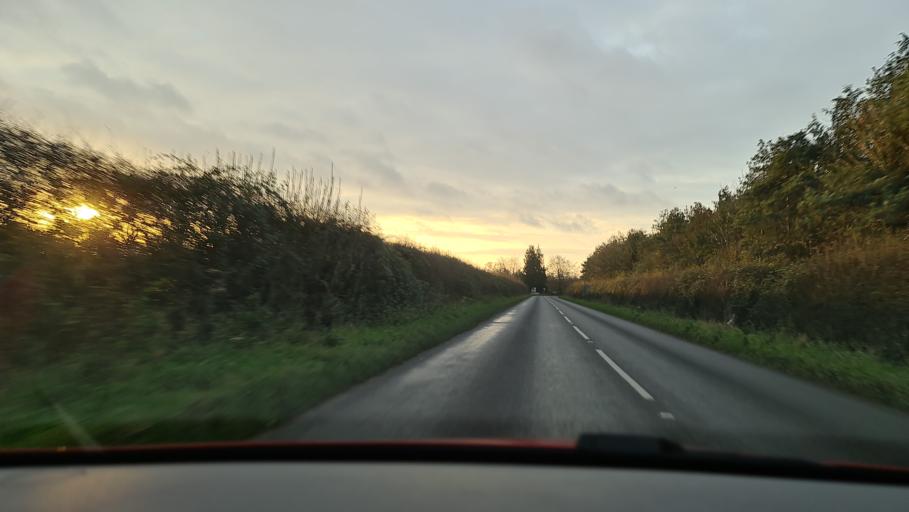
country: GB
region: England
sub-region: Oxfordshire
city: Kidlington
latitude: 51.8824
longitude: -1.2741
